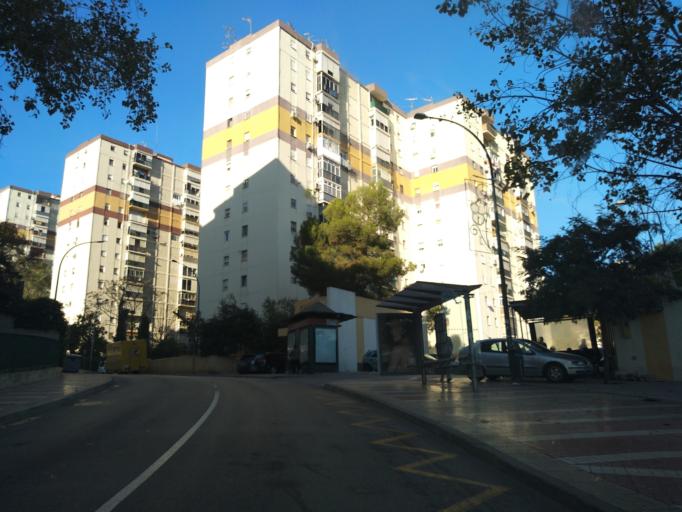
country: ES
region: Andalusia
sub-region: Provincia de Malaga
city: Malaga
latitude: 36.7416
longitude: -4.4312
